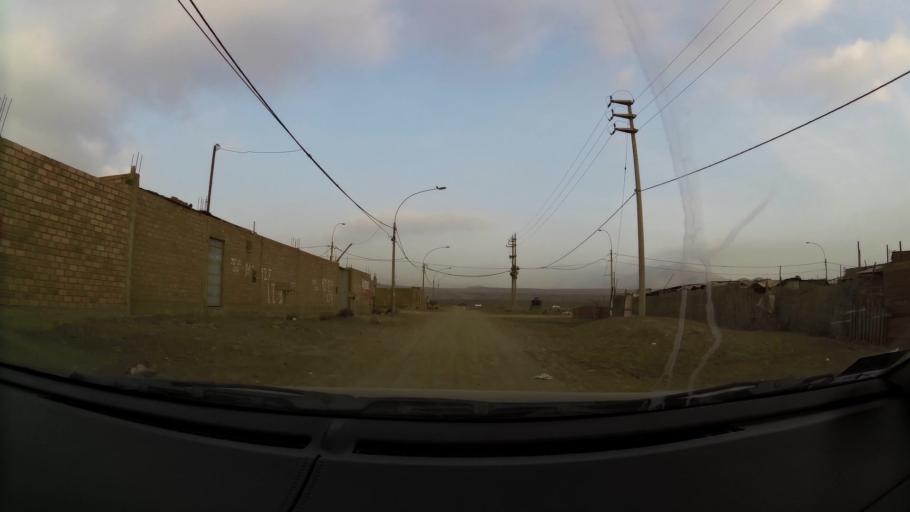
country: PE
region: Lima
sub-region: Lima
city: Santa Rosa
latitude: -11.7391
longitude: -77.1391
